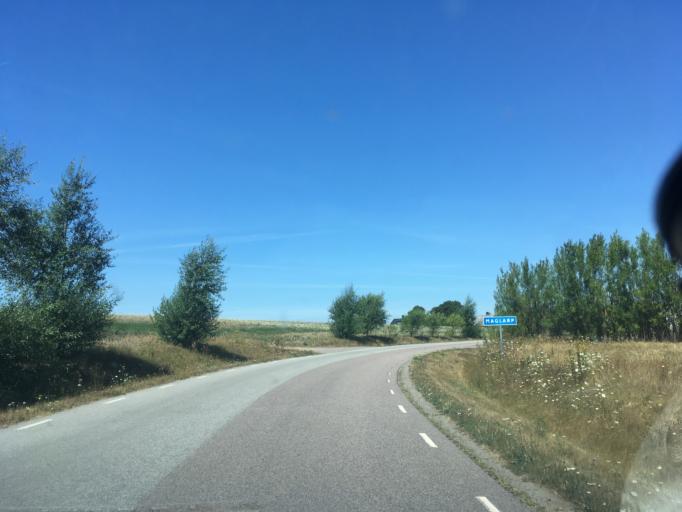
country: SE
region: Skane
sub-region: Trelleborgs Kommun
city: Skare
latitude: 55.3858
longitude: 13.0825
